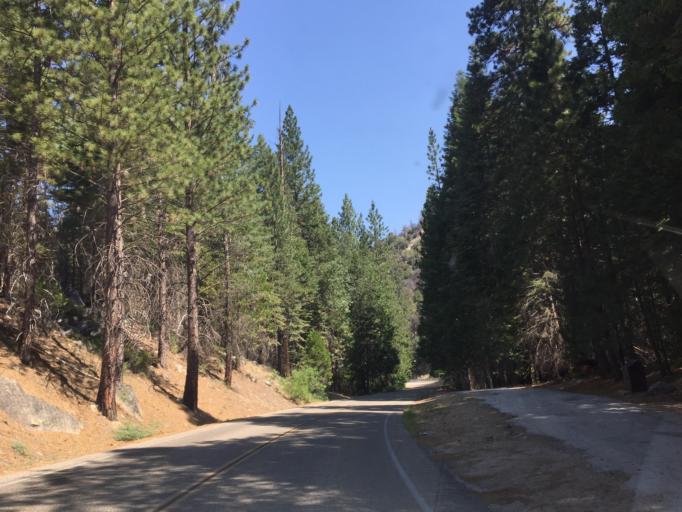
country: US
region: California
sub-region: Tulare County
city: Three Rivers
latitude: 36.7959
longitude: -118.6864
